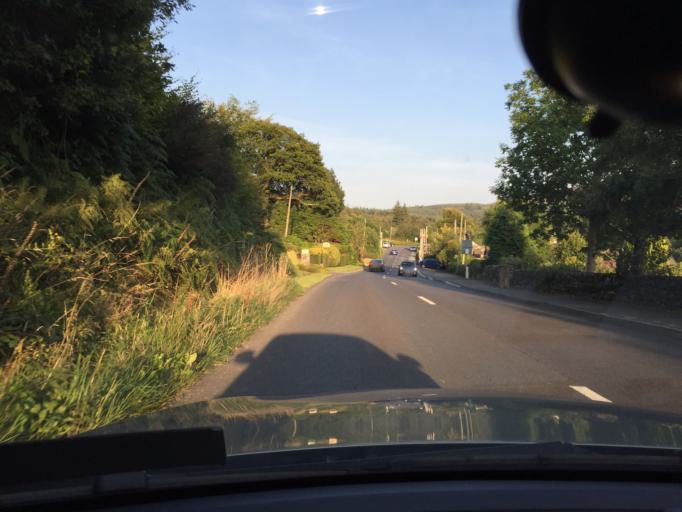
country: IE
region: Leinster
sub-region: Wicklow
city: Rathdrum
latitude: 53.0091
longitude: -6.3023
